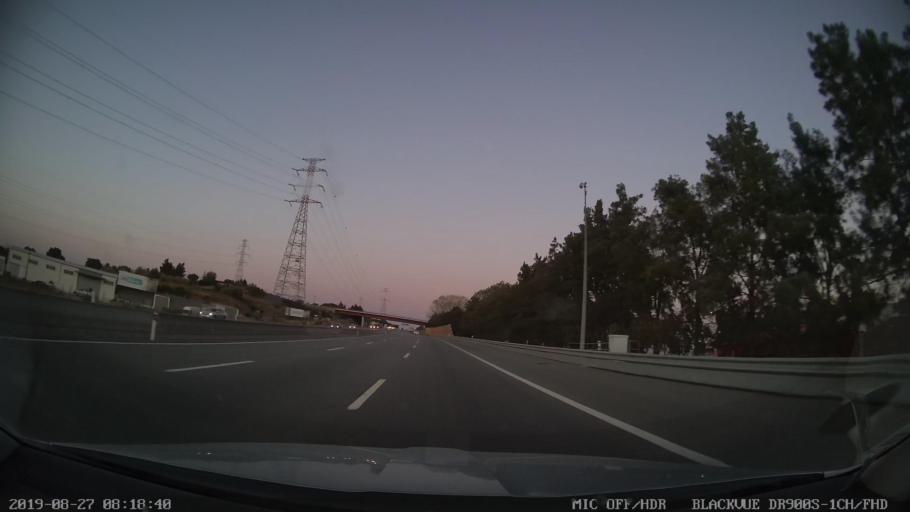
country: PT
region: Setubal
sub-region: Palmela
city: Palmela
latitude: 38.5847
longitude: -8.9088
